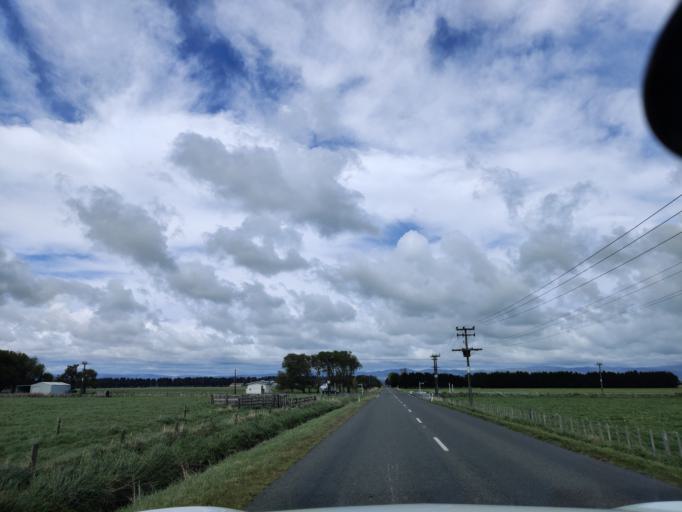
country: NZ
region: Manawatu-Wanganui
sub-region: Palmerston North City
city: Palmerston North
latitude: -40.3335
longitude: 175.5148
